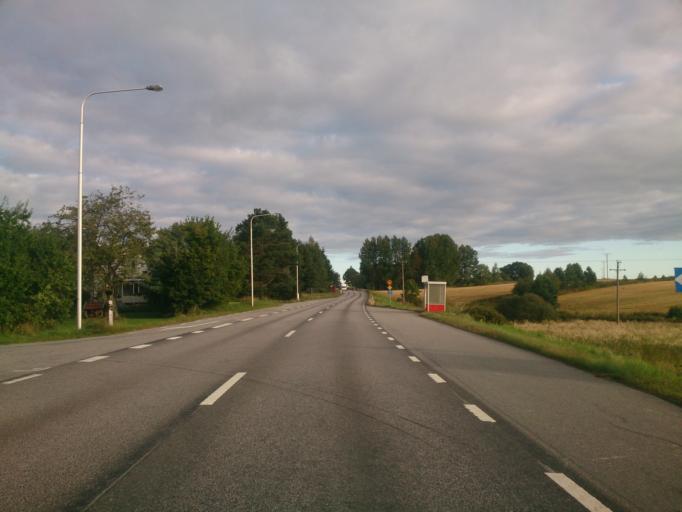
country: SE
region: OEstergoetland
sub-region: Linkopings Kommun
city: Sturefors
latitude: 58.3146
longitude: 15.8729
